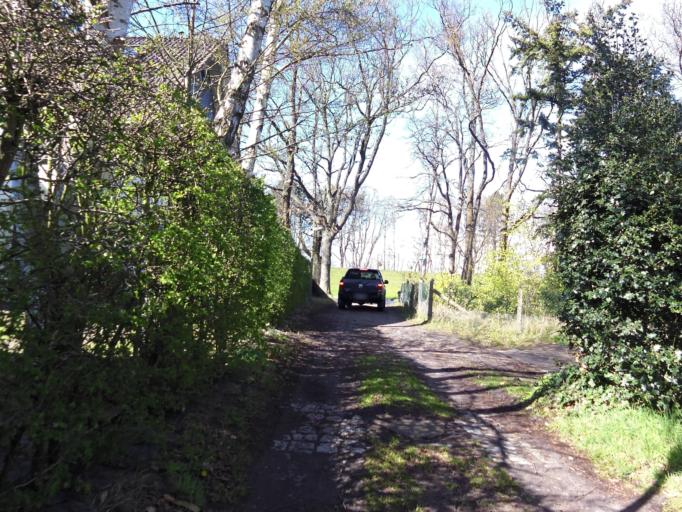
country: DE
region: Mecklenburg-Vorpommern
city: Zingst
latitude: 54.4408
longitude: 12.7012
